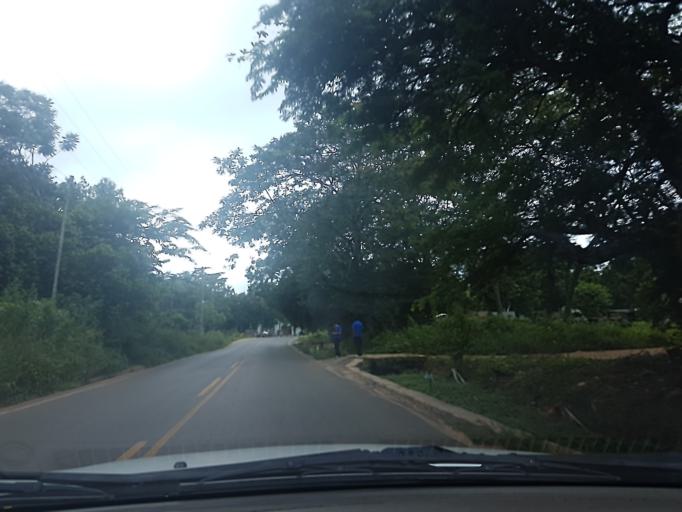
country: PY
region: Central
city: Limpio
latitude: -25.1967
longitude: -57.4560
